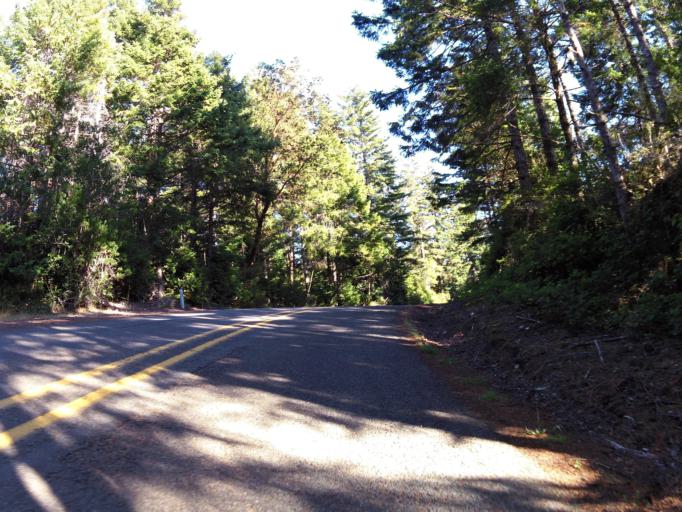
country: US
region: Oregon
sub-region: Coos County
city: Bandon
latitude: 43.0364
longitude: -124.3921
